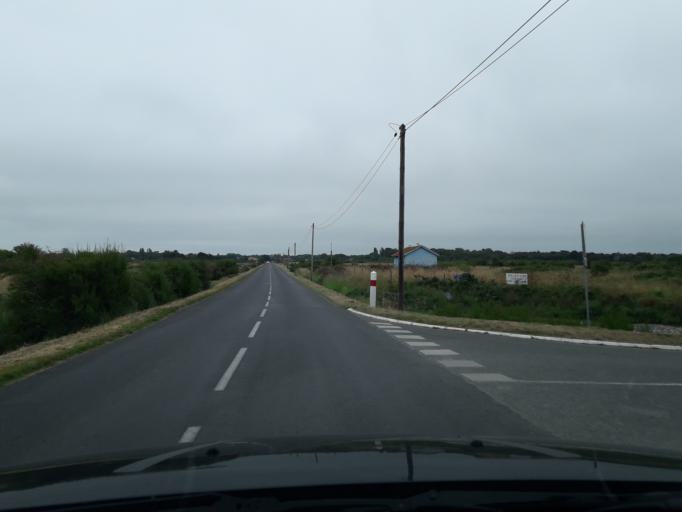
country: FR
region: Poitou-Charentes
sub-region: Departement de la Charente-Maritime
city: Boyard-Ville
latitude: 45.9605
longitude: -1.2492
